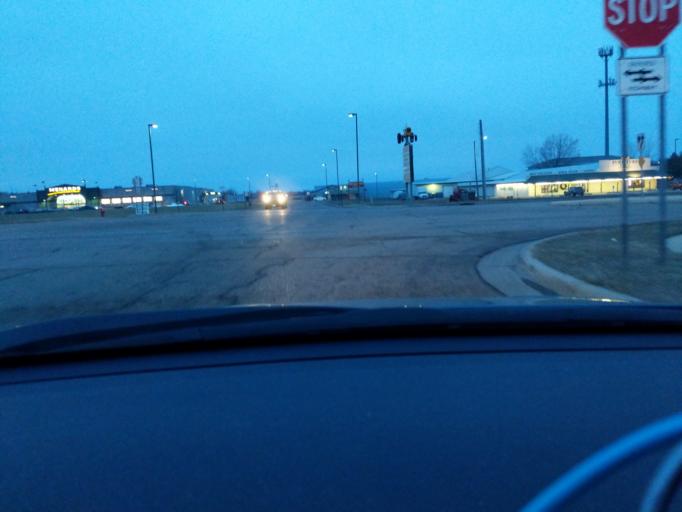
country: US
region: Minnesota
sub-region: Kandiyohi County
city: Willmar
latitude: 45.0945
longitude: -95.0422
